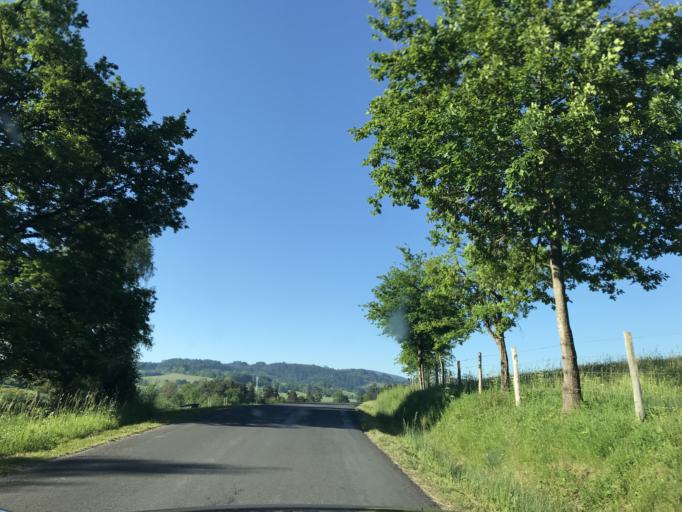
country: FR
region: Auvergne
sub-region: Departement du Puy-de-Dome
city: Job
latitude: 45.6573
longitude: 3.6742
